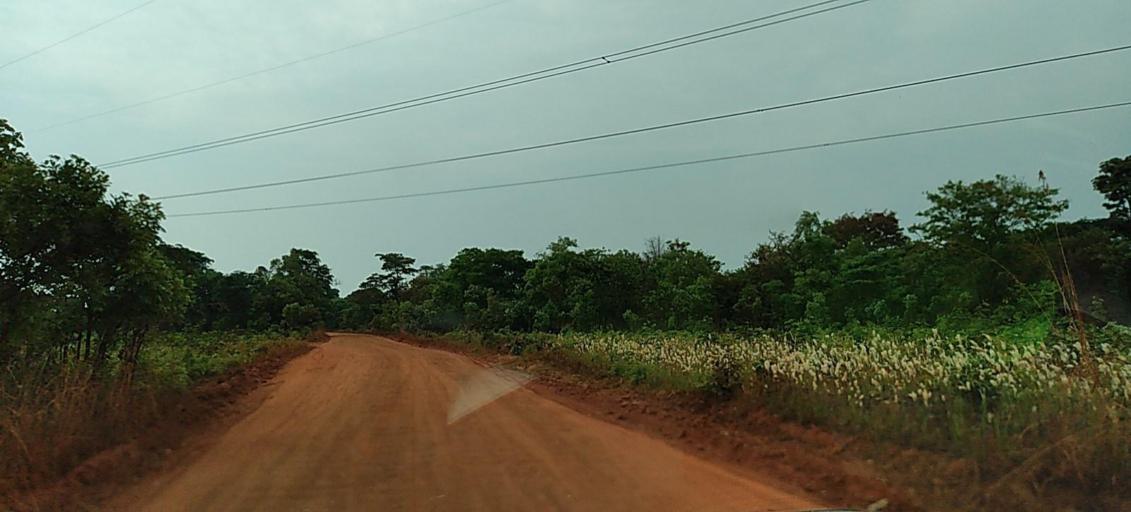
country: ZM
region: North-Western
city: Solwezi
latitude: -12.2148
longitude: 26.5058
